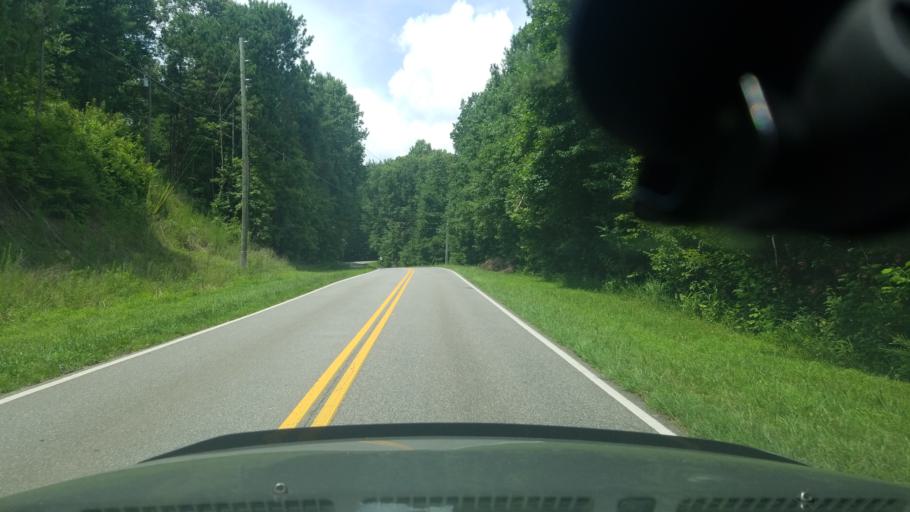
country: US
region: Georgia
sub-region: Forsyth County
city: Cumming
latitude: 34.2918
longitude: -84.2413
